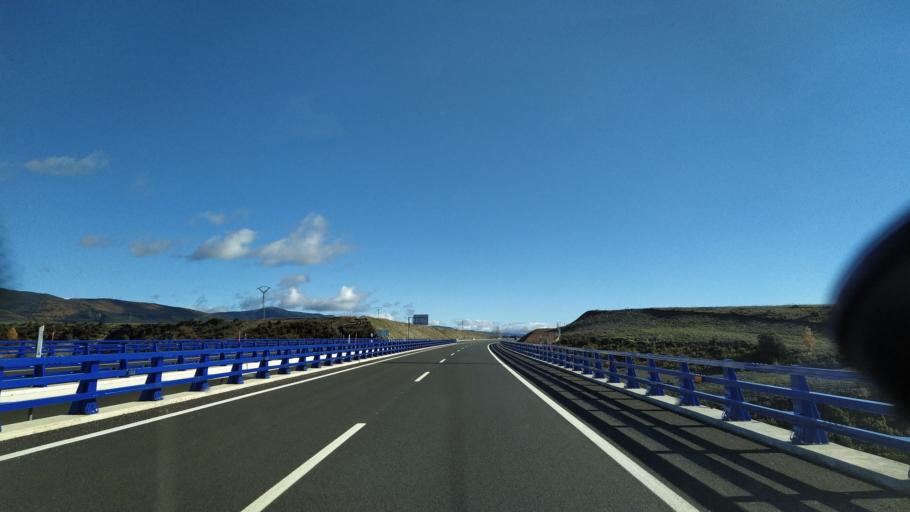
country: ES
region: Aragon
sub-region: Provincia de Huesca
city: Santa Cruz de la Seros
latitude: 42.5638
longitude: -0.6327
